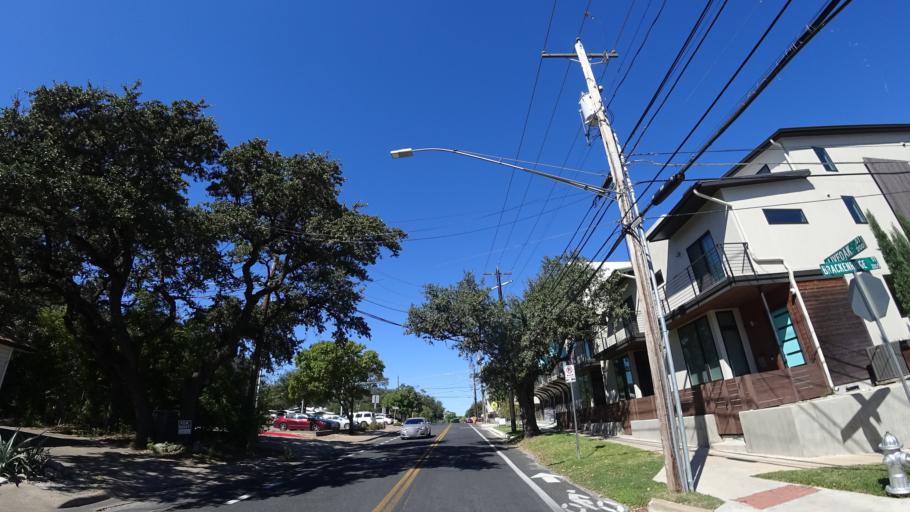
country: US
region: Texas
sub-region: Travis County
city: Austin
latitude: 30.2411
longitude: -97.7506
